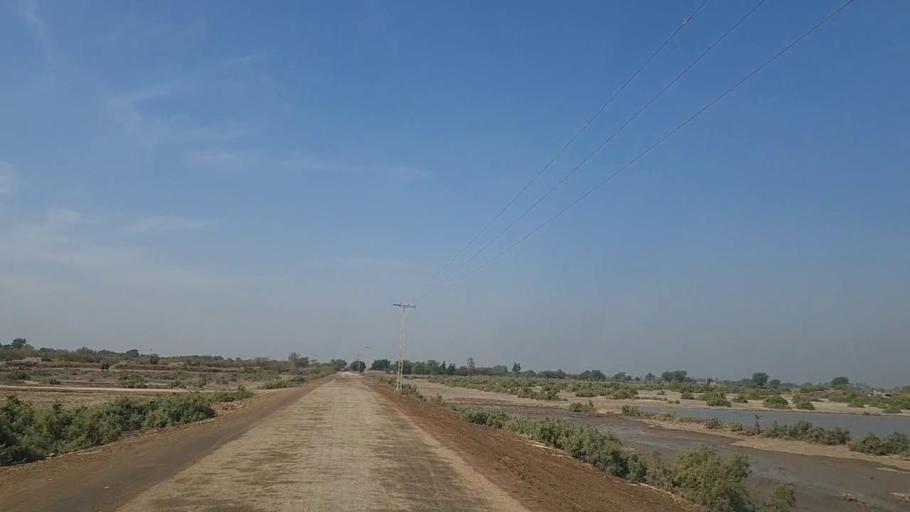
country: PK
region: Sindh
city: Mirpur Khas
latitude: 25.4825
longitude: 68.9776
